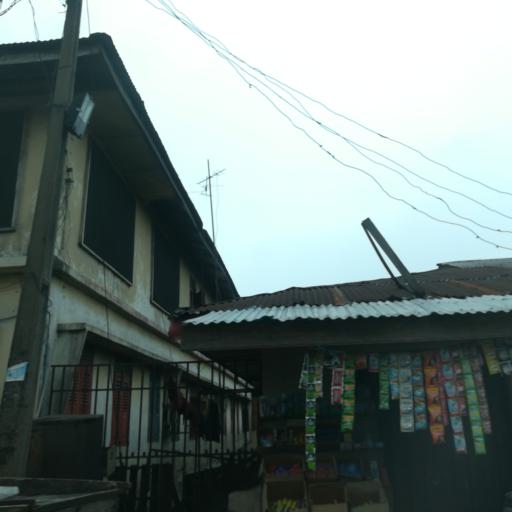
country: NG
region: Rivers
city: Port Harcourt
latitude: 4.8025
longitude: 6.9918
